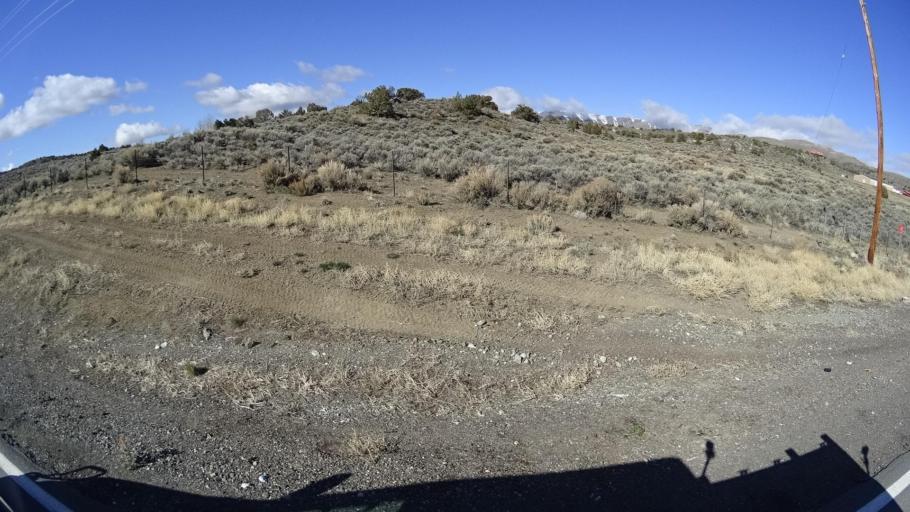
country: US
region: Nevada
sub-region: Washoe County
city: Cold Springs
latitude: 39.7464
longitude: -119.8858
